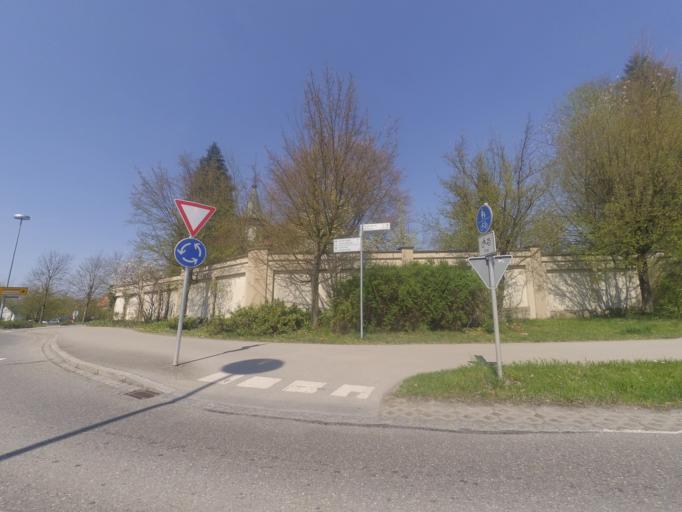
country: DE
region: Bavaria
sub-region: Swabia
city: Weissenhorn
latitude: 48.2991
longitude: 10.1609
